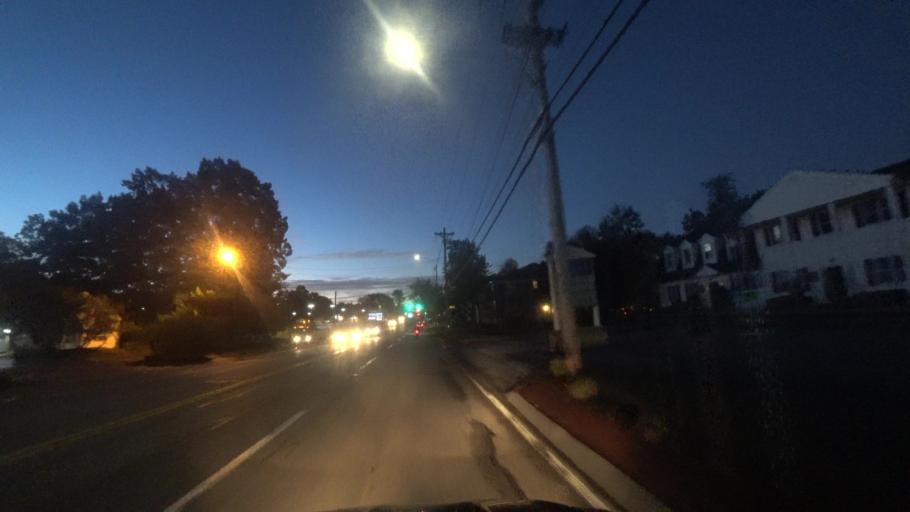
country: US
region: Massachusetts
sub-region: Middlesex County
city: North Reading
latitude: 42.5936
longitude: -71.1188
